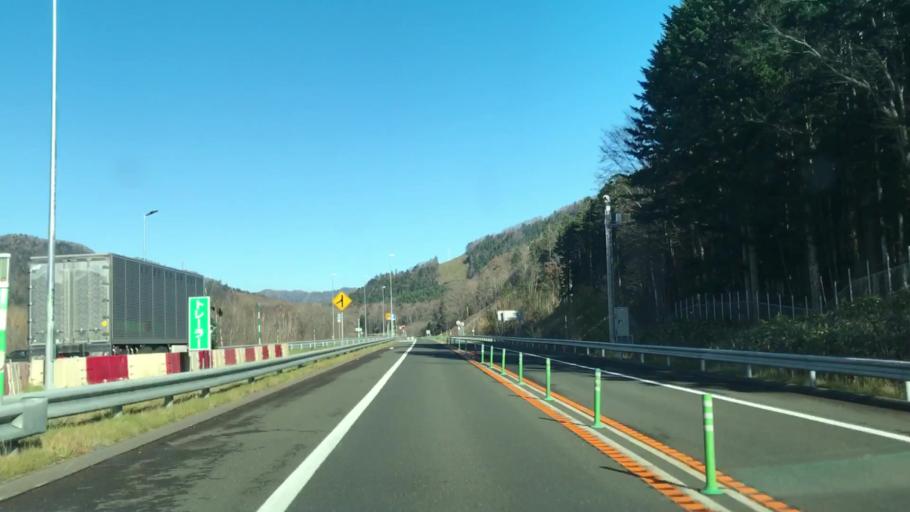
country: JP
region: Hokkaido
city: Shimo-furano
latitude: 43.0092
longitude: 142.4226
